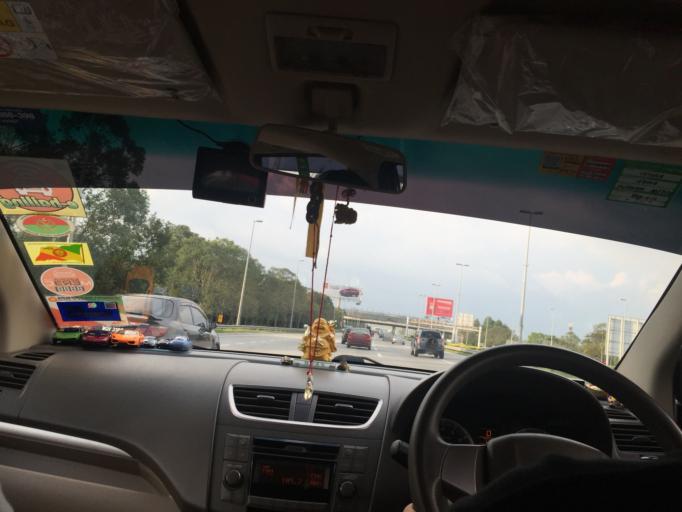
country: MY
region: Negeri Sembilan
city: Kampung Baharu Nilai
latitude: 2.7854
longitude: 101.6734
